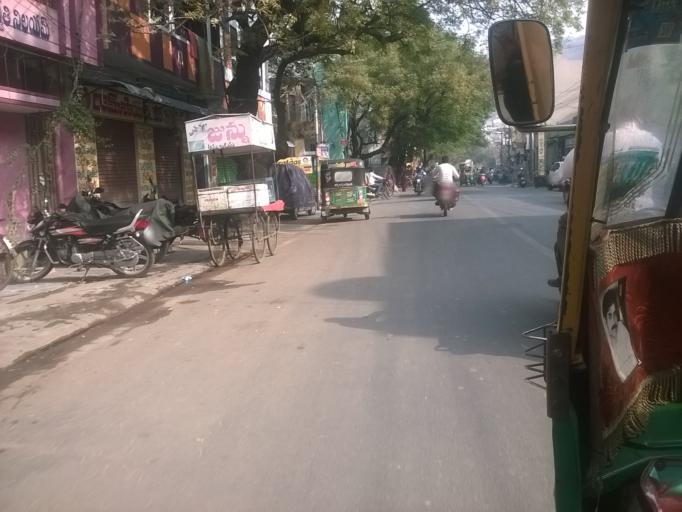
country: IN
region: Andhra Pradesh
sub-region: Krishna
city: Vijayawada
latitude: 16.5292
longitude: 80.6053
